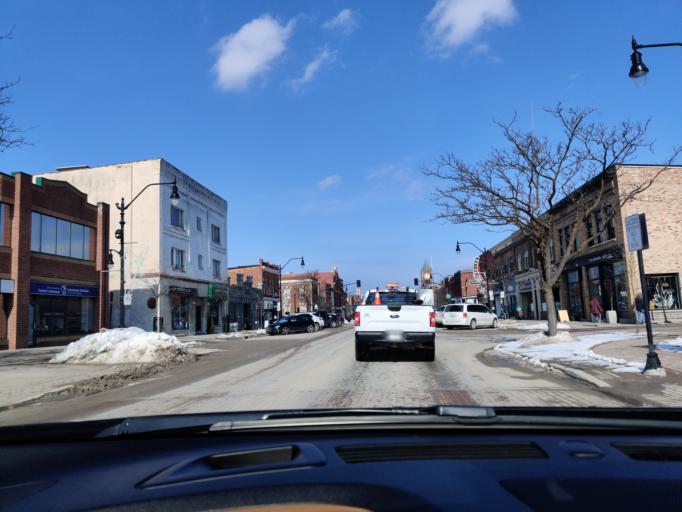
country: CA
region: Ontario
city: Collingwood
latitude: 44.4980
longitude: -80.2165
